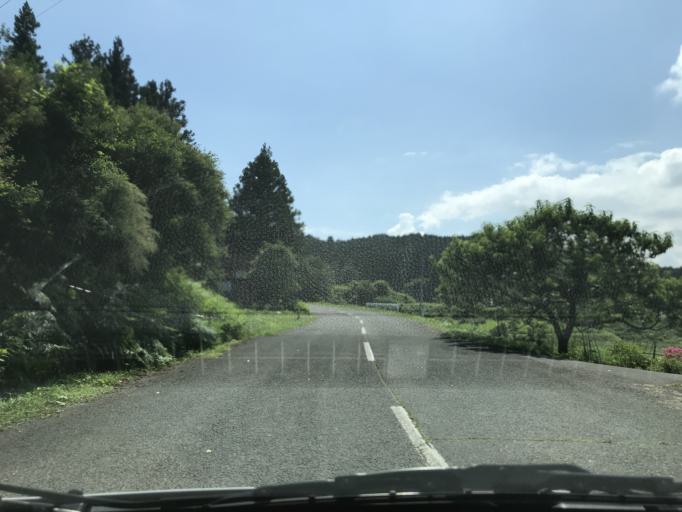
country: JP
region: Iwate
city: Ofunato
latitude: 38.9934
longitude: 141.4294
